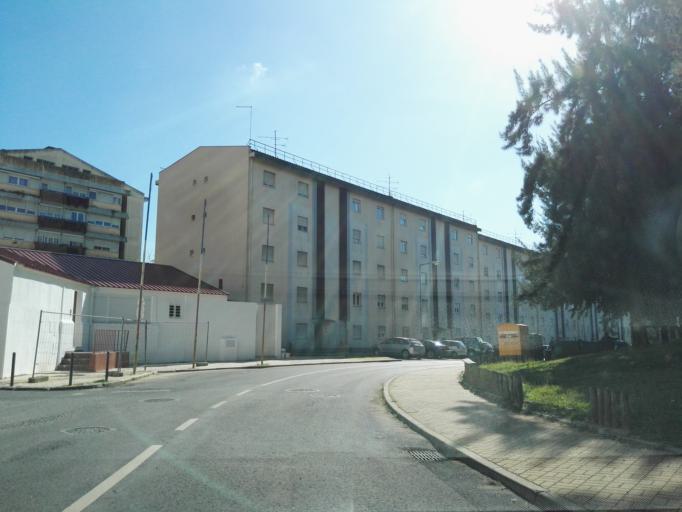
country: PT
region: Lisbon
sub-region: Amadora
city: Amadora
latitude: 38.7335
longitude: -9.2062
